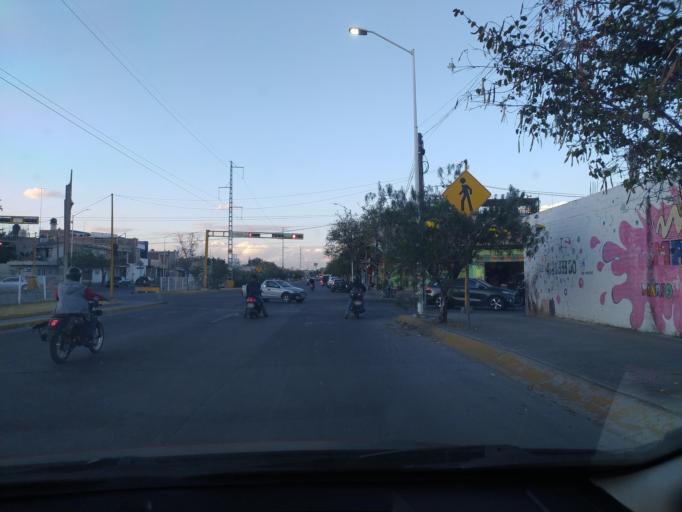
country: LA
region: Oudomxai
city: Muang La
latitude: 21.0243
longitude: 101.8694
